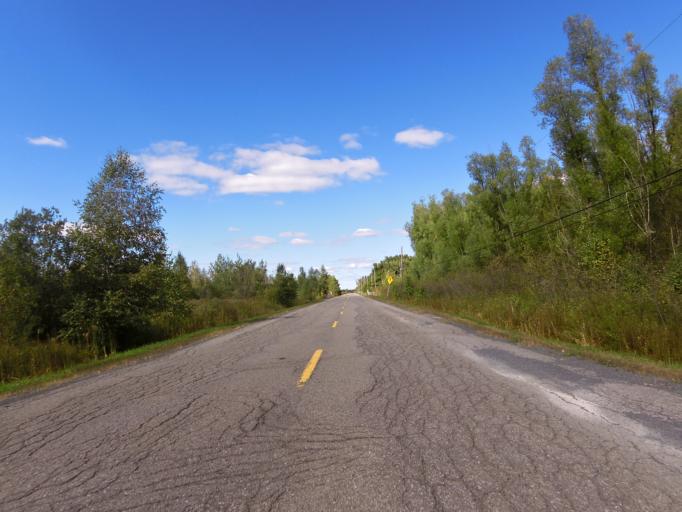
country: CA
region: Ontario
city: Ottawa
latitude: 45.3220
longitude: -75.4864
